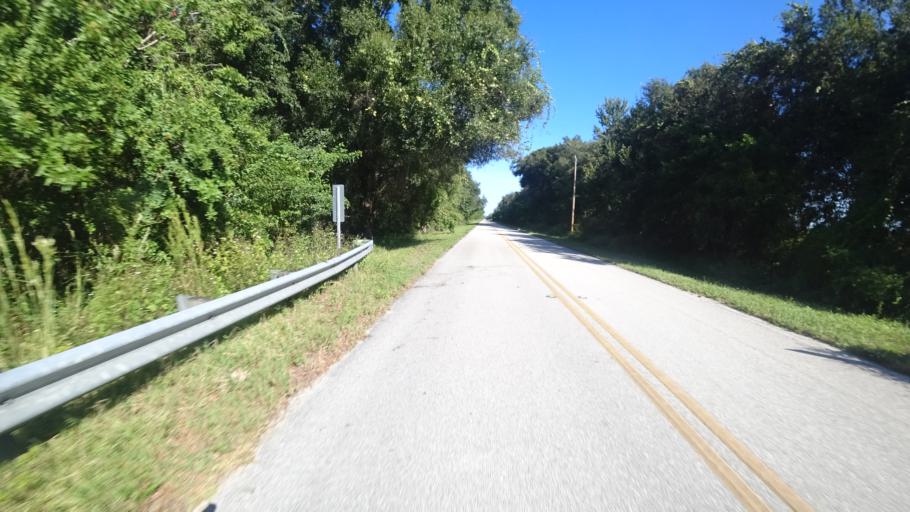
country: US
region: Florida
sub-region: Hillsborough County
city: Wimauma
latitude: 27.6268
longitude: -82.2925
